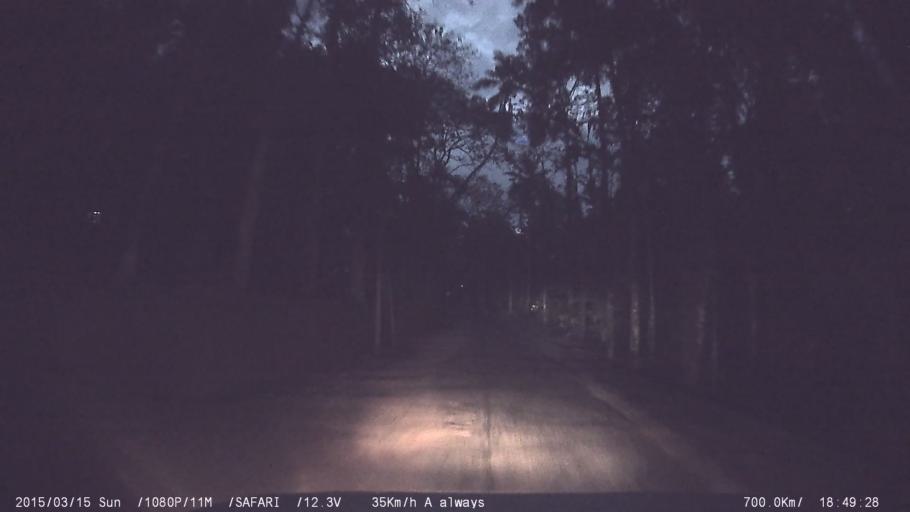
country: IN
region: Kerala
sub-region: Kottayam
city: Palackattumala
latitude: 9.8551
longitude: 76.6973
